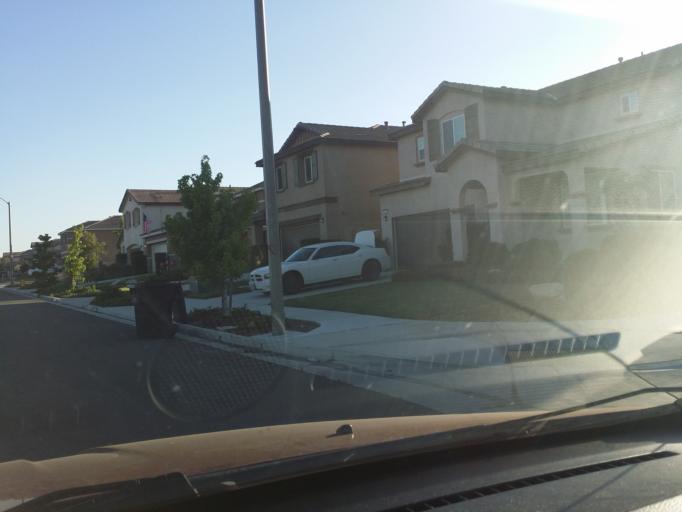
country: US
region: California
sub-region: San Bernardino County
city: Muscoy
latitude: 34.1909
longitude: -117.4208
